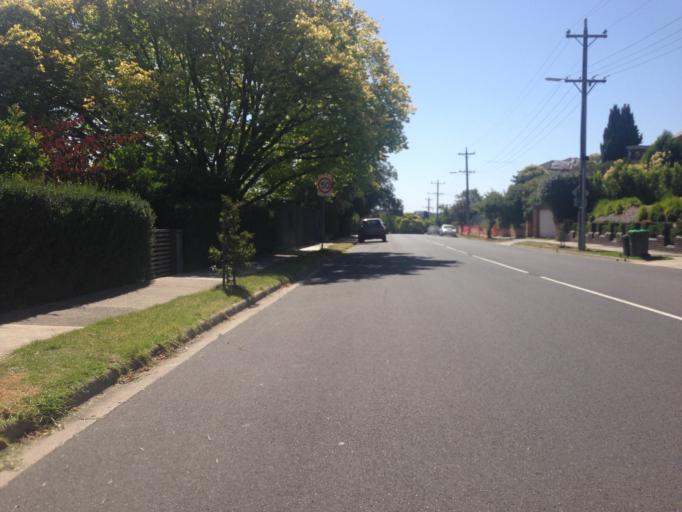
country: AU
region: Victoria
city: Ivanhoe East
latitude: -37.7781
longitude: 145.0568
